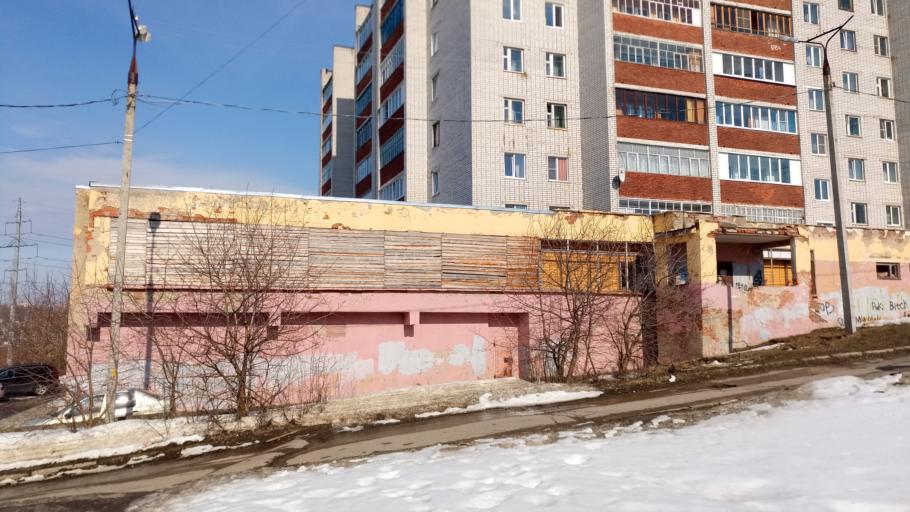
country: RU
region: Chuvashia
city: Novyye Lapsary
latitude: 56.1241
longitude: 47.1870
